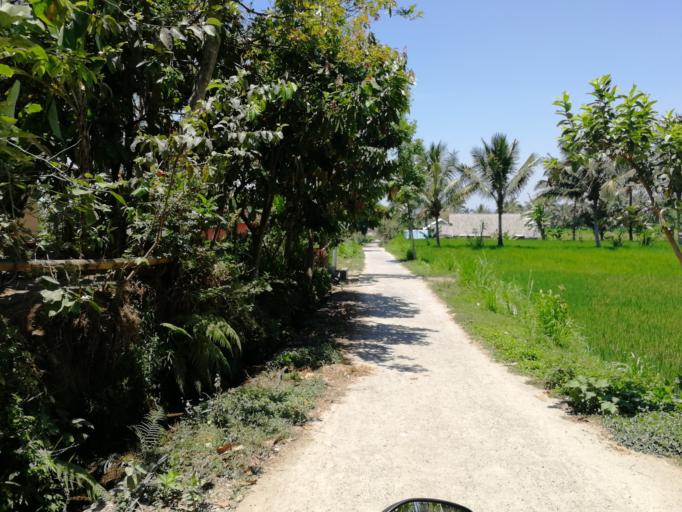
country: ID
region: West Nusa Tenggara
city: Tetebatu
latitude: -8.5416
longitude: 116.4206
